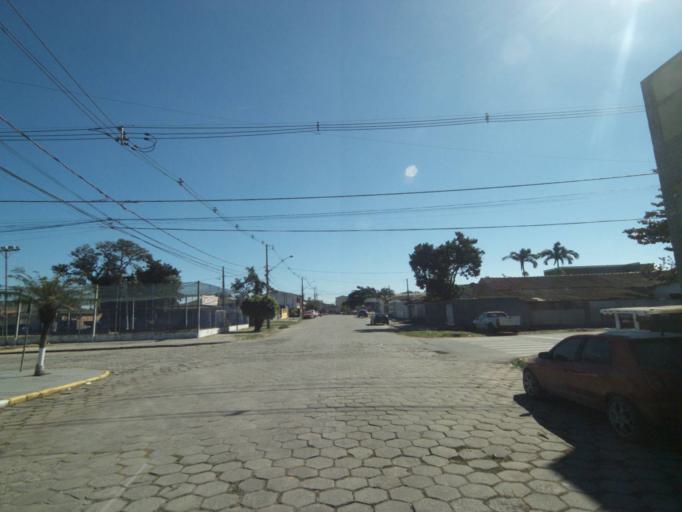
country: BR
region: Parana
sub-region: Paranagua
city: Paranagua
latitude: -25.5120
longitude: -48.5022
